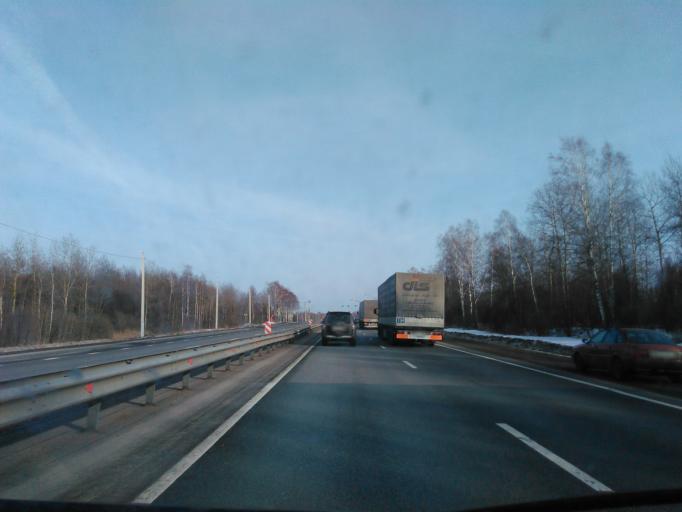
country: RU
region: Smolensk
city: Verkhnedneprovskiy
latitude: 55.1819
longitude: 33.5585
